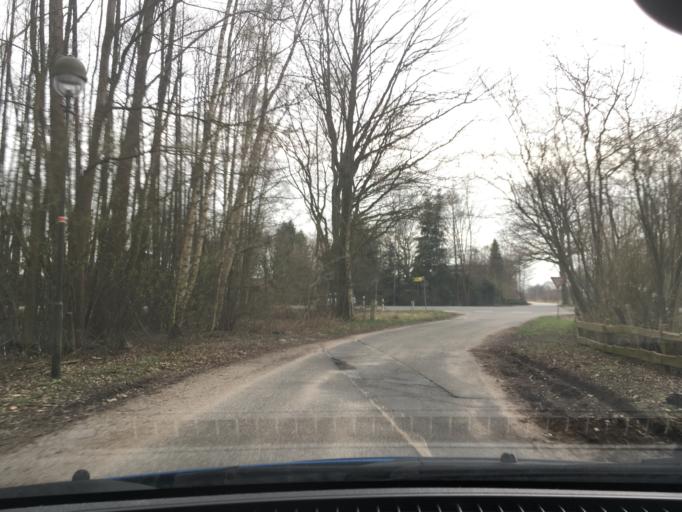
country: DE
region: Lower Saxony
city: Tespe
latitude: 53.3911
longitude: 10.4284
